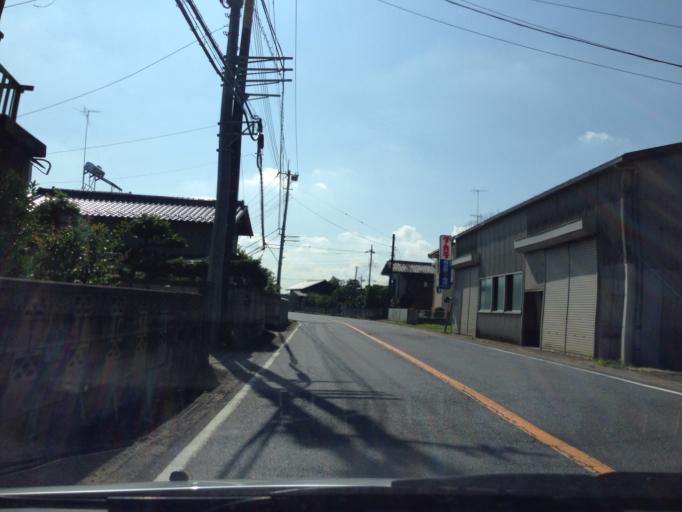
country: JP
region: Ibaraki
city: Ami
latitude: 36.0280
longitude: 140.2773
